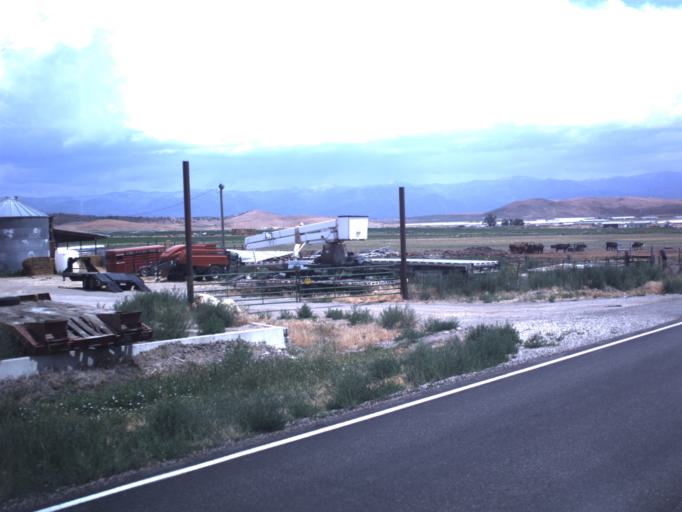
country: US
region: Utah
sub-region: Sanpete County
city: Moroni
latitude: 39.5746
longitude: -111.6091
